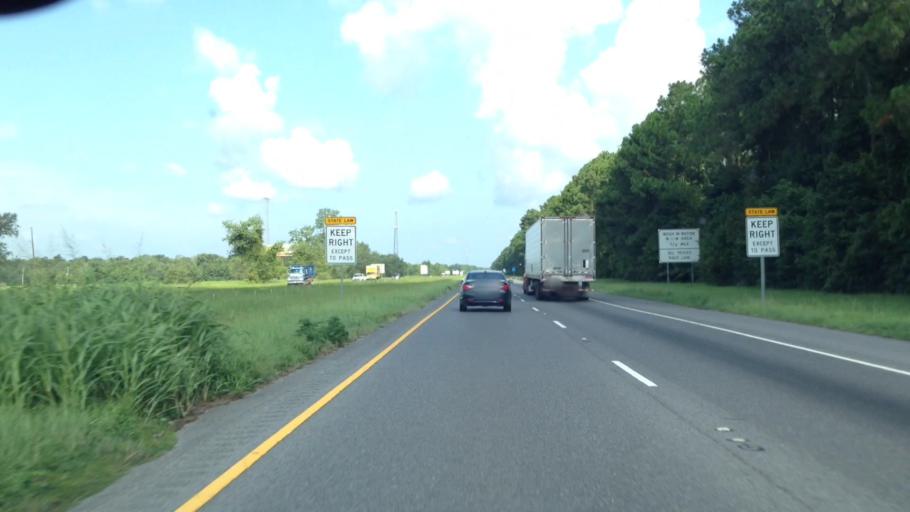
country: US
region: Louisiana
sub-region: Saint John the Baptist Parish
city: Laplace
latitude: 30.0924
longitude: -90.4551
